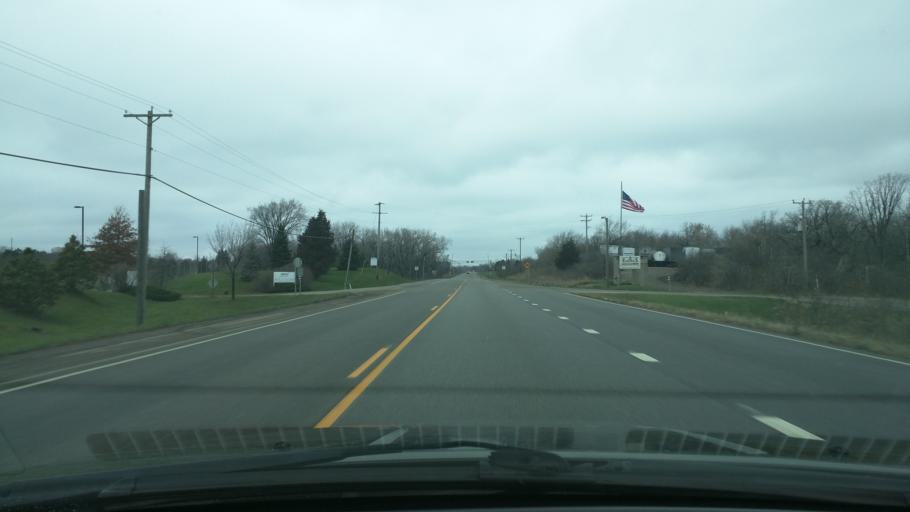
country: US
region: Minnesota
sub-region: Washington County
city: Saint Paul Park
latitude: 44.7538
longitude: -93.0076
